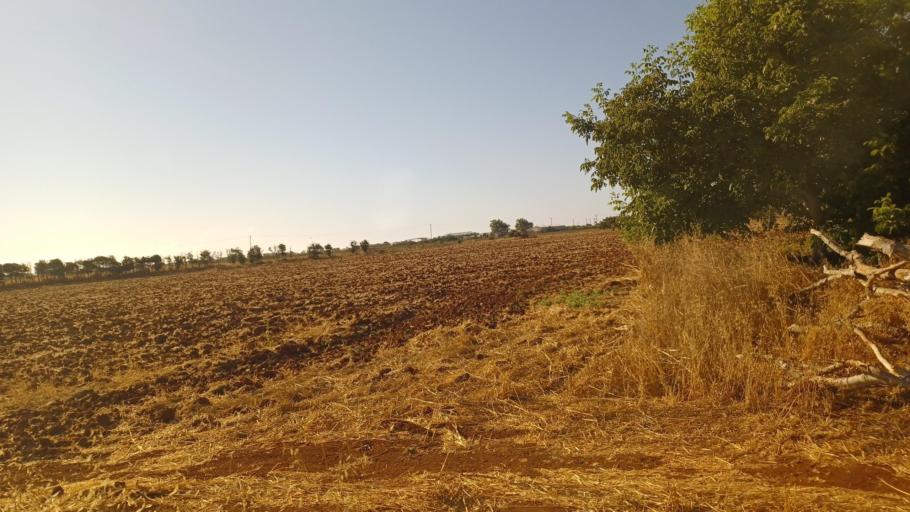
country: CY
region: Ammochostos
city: Avgorou
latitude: 35.0159
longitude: 33.8402
